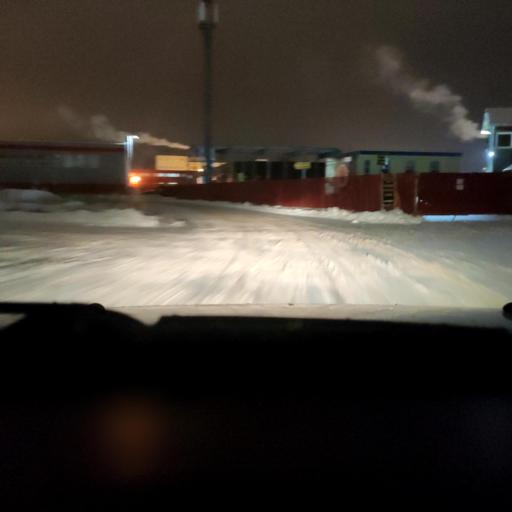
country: RU
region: Perm
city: Froly
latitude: 57.9569
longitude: 56.2724
